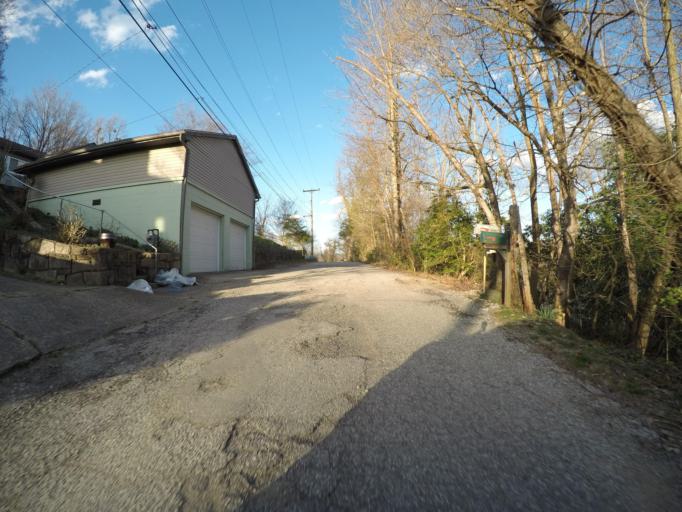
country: US
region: West Virginia
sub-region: Kanawha County
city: Charleston
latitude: 38.3893
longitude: -81.5965
